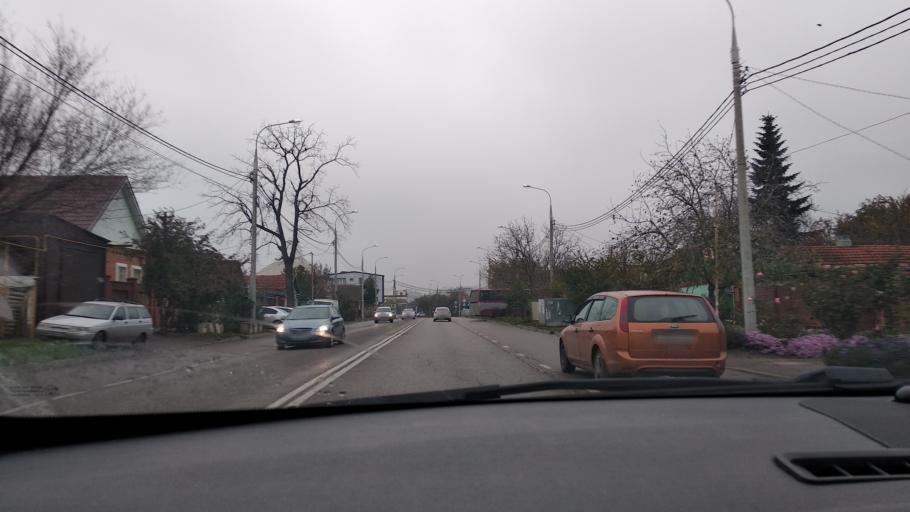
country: RU
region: Krasnodarskiy
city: Krasnodar
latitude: 45.0116
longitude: 39.0091
